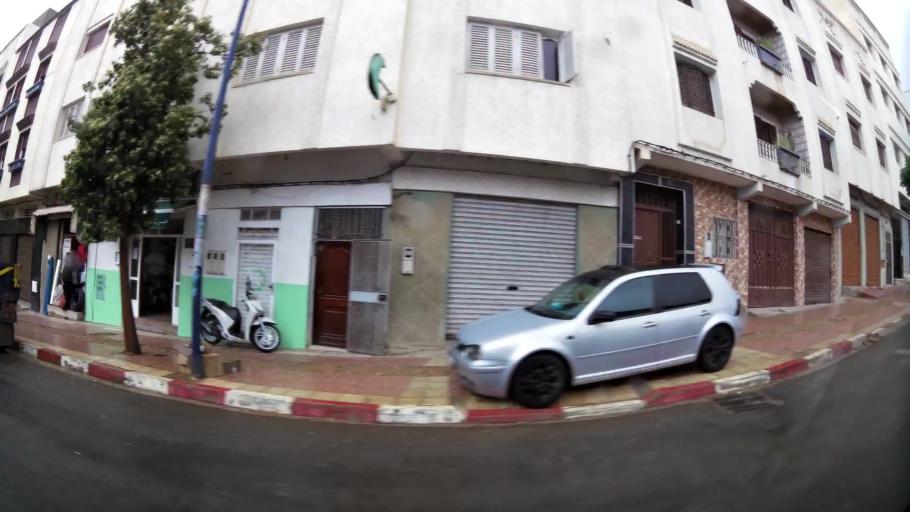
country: MA
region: Taza-Al Hoceima-Taounate
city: Al Hoceima
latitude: 35.2519
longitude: -3.9343
